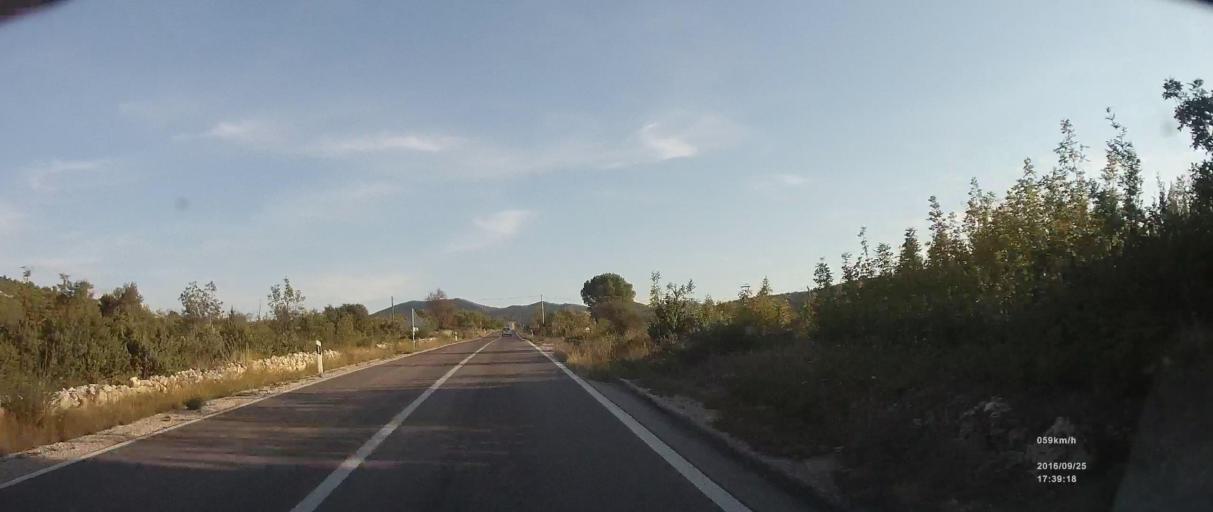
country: HR
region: Sibensko-Kniniska
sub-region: Grad Sibenik
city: Brodarica
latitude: 43.6463
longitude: 16.0617
